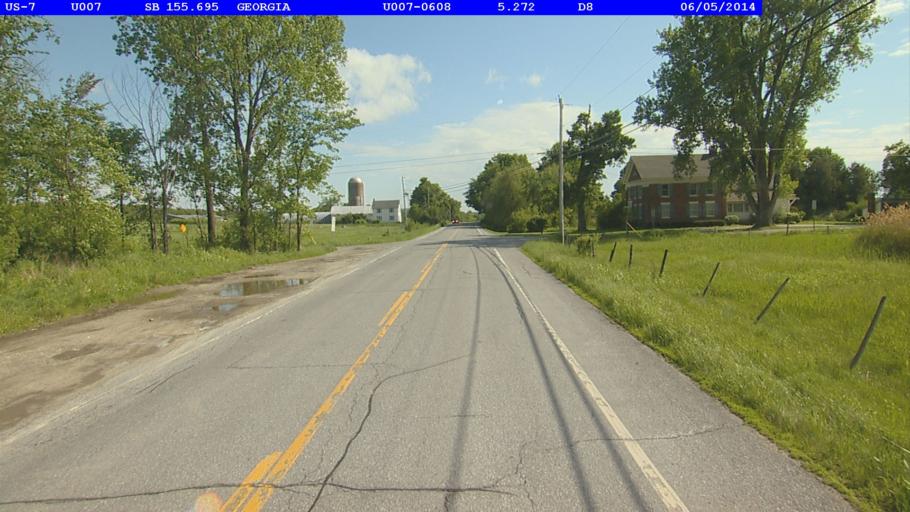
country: US
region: Vermont
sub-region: Franklin County
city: Saint Albans
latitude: 44.7471
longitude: -73.1132
